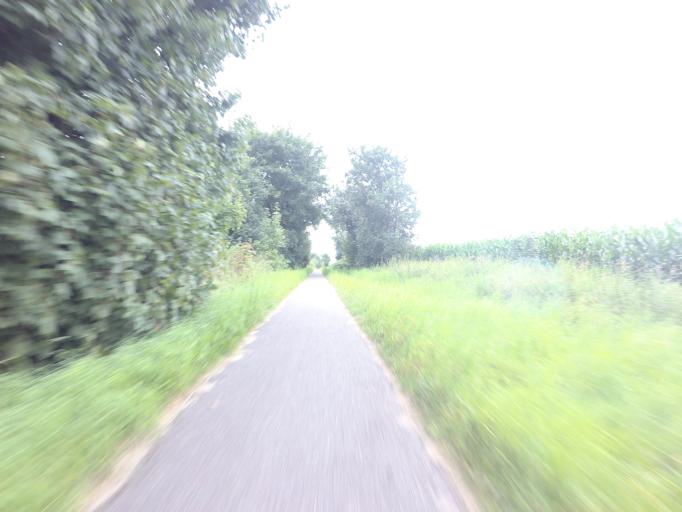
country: DK
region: Central Jutland
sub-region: Horsens Kommune
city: Braedstrup
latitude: 56.0102
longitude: 9.5857
